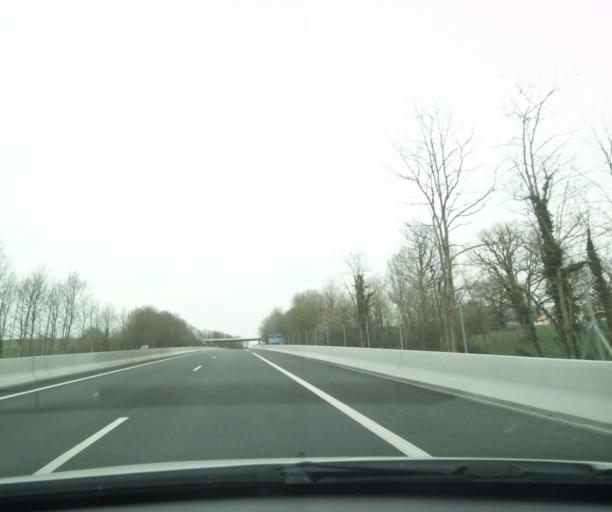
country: FR
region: Aquitaine
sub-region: Departement des Pyrenees-Atlantiques
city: Briscous
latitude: 43.4515
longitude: -1.3472
